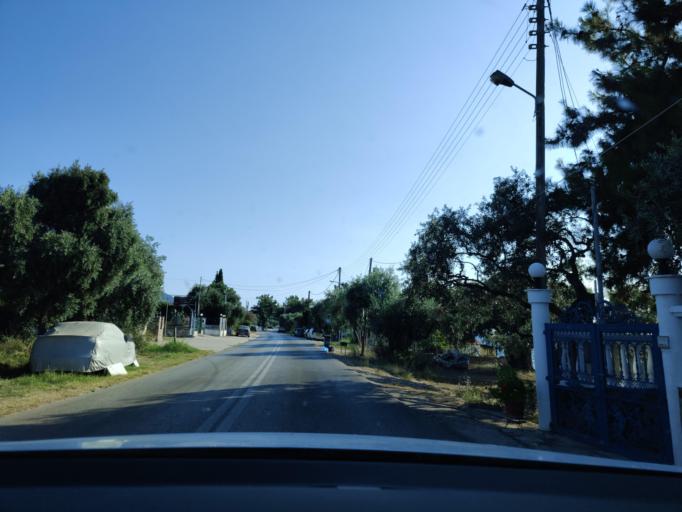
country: GR
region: East Macedonia and Thrace
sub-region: Nomos Kavalas
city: Prinos
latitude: 40.7017
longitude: 24.5292
